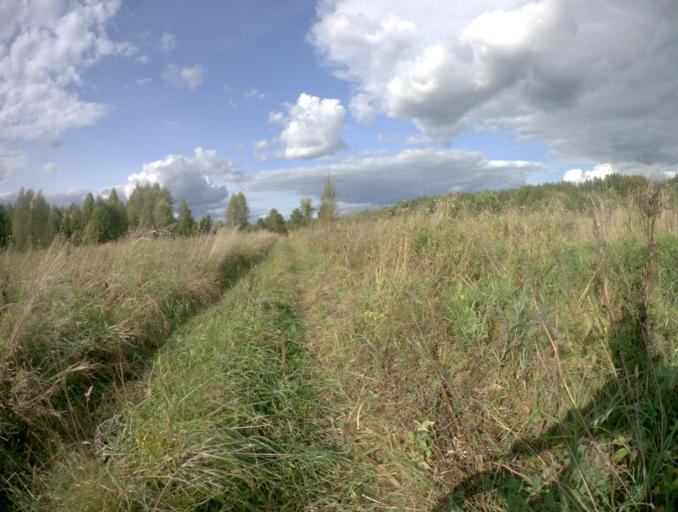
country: RU
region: Vladimir
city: Ivanishchi
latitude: 55.8523
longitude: 40.3975
